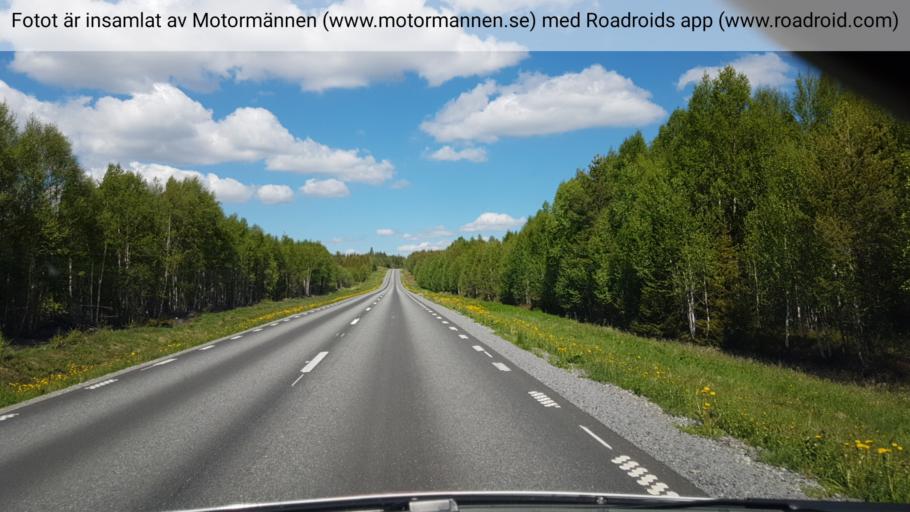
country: SE
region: Vaesterbotten
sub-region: Vilhelmina Kommun
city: Vilhelmina
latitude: 64.7067
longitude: 16.7078
